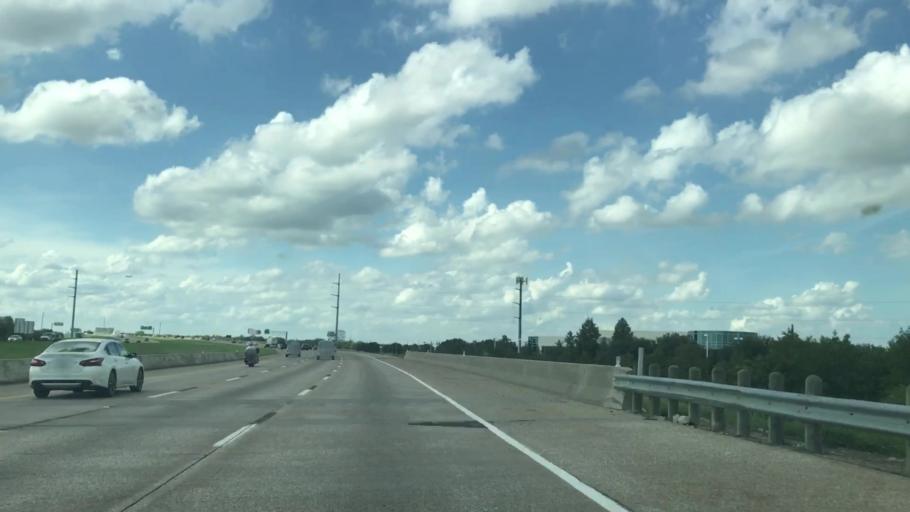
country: US
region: Texas
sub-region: Dallas County
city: Coppell
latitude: 32.9413
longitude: -97.0131
